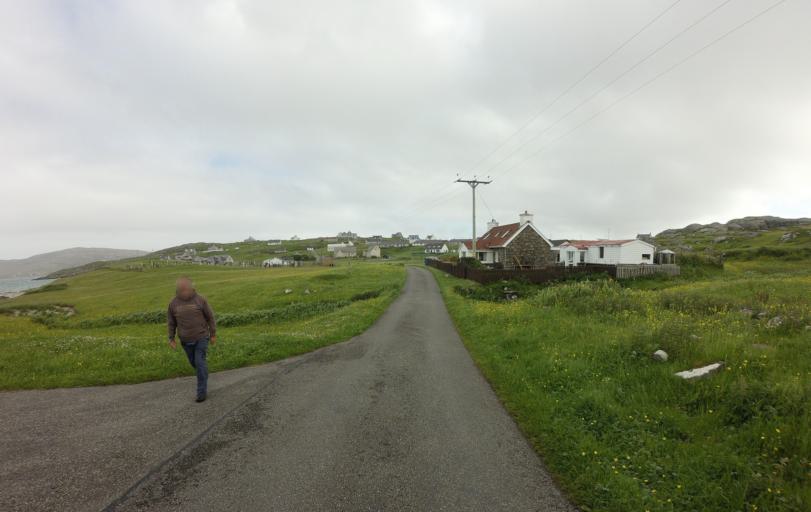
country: GB
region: Scotland
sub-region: Eilean Siar
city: Isle of South Uist
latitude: 57.0826
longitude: -7.3097
